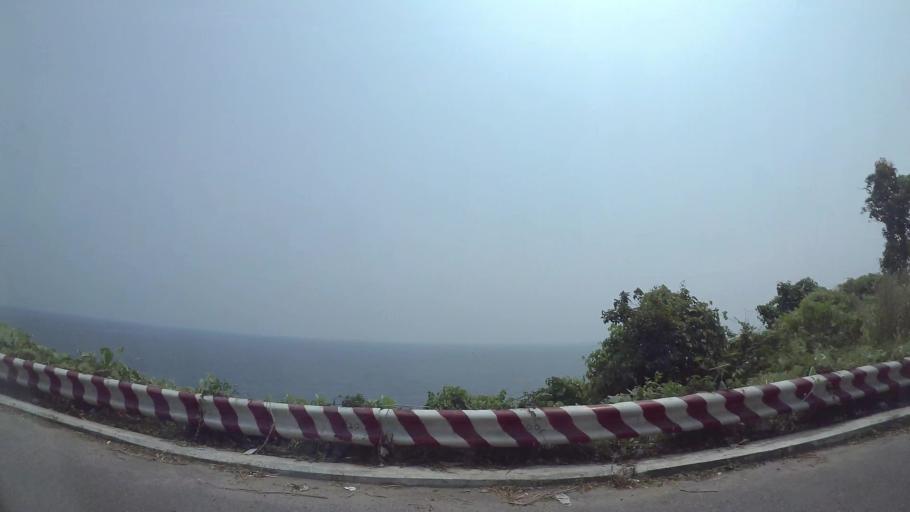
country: VN
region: Da Nang
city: Son Tra
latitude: 16.0983
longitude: 108.2770
